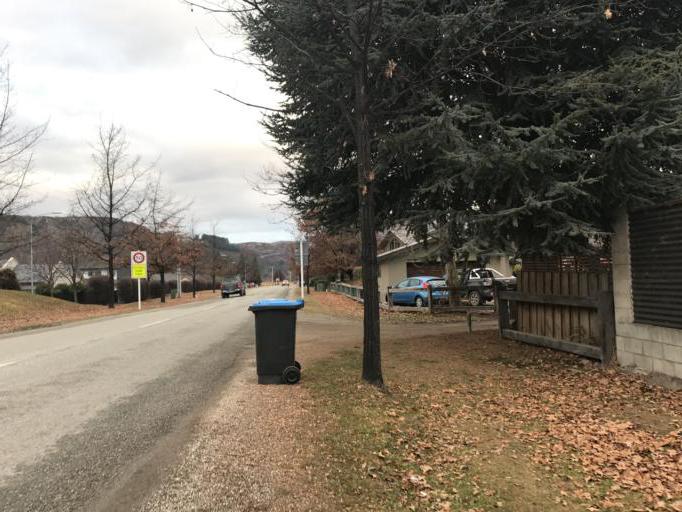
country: NZ
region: Otago
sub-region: Queenstown-Lakes District
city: Arrowtown
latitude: -44.9502
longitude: 168.8419
